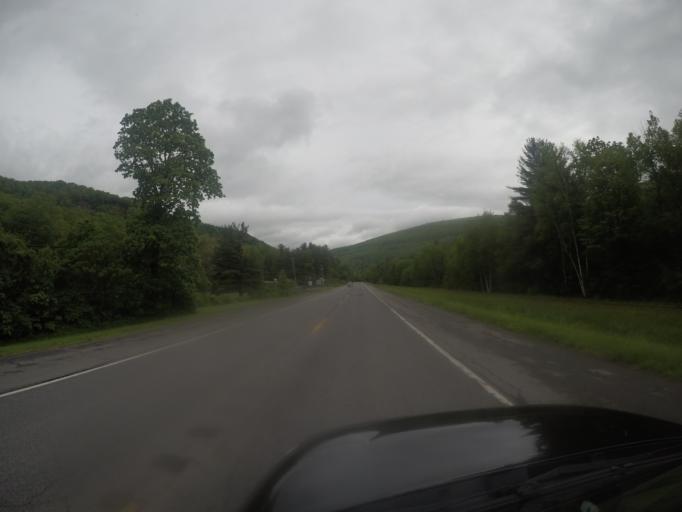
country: US
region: New York
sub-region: Ulster County
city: Shokan
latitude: 42.0698
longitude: -74.3073
